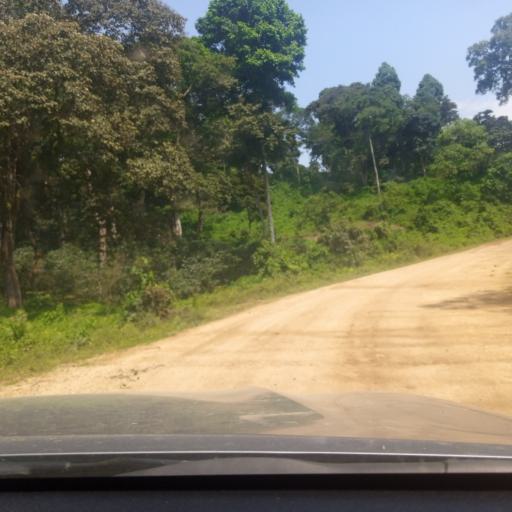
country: ET
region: Southern Nations, Nationalities, and People's Region
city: Tippi
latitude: 7.0713
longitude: 35.4346
